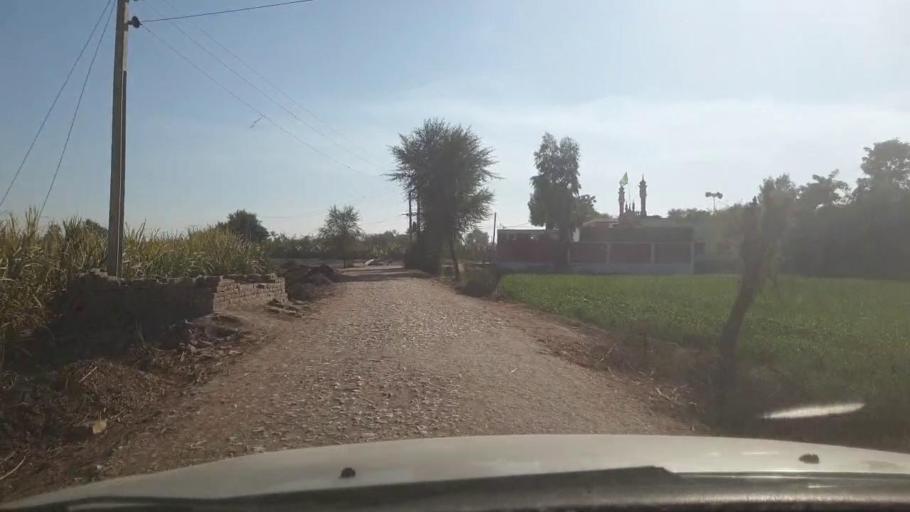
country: PK
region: Sindh
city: Ghotki
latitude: 27.9753
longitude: 69.1872
